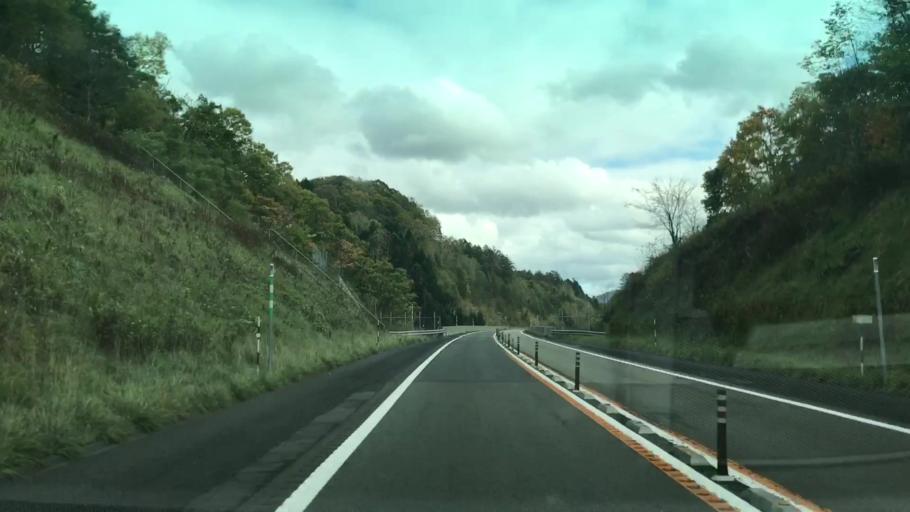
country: JP
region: Hokkaido
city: Chitose
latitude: 42.9146
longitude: 141.9709
